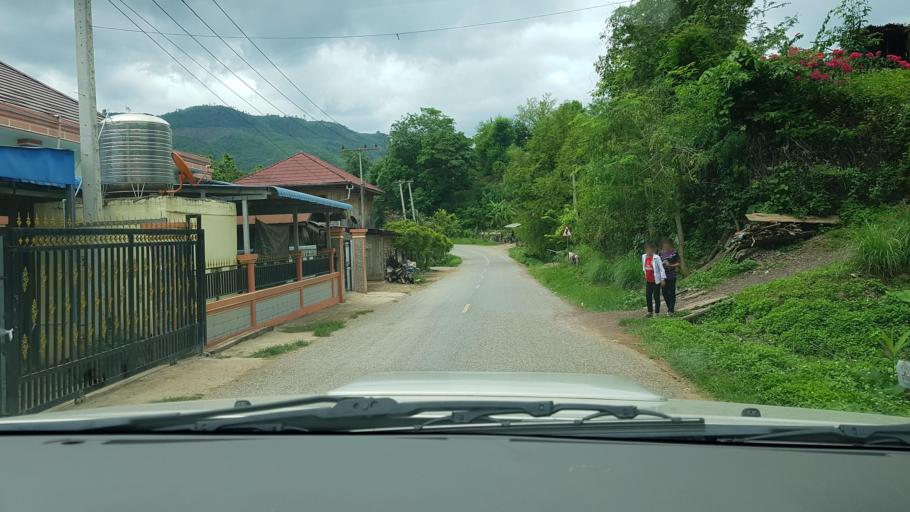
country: TH
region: Nan
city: Chaloem Phra Kiat
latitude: 19.9650
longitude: 101.2631
